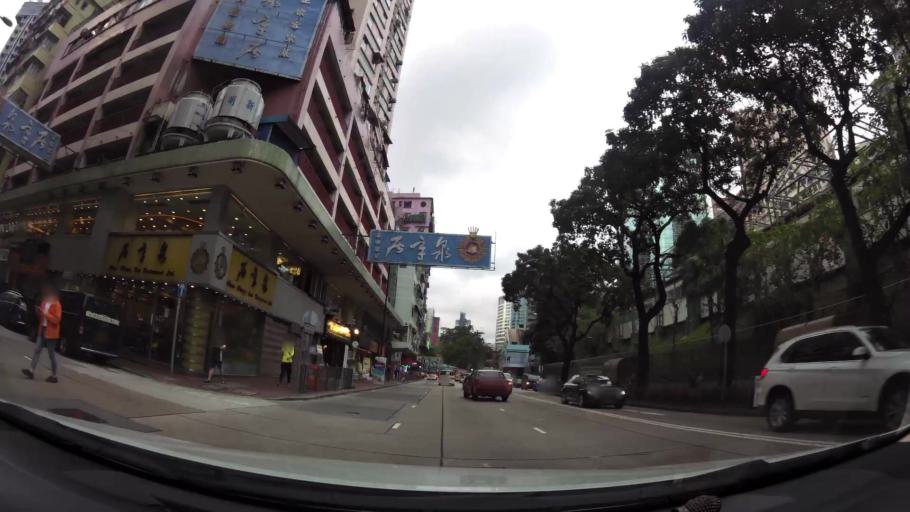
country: HK
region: Kowloon City
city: Kowloon
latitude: 22.3189
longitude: 114.1731
